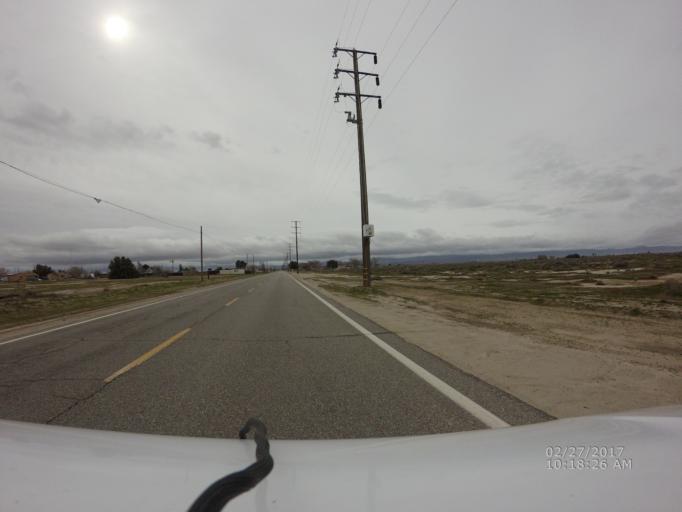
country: US
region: California
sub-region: Los Angeles County
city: Lancaster
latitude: 34.7502
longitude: -118.1310
